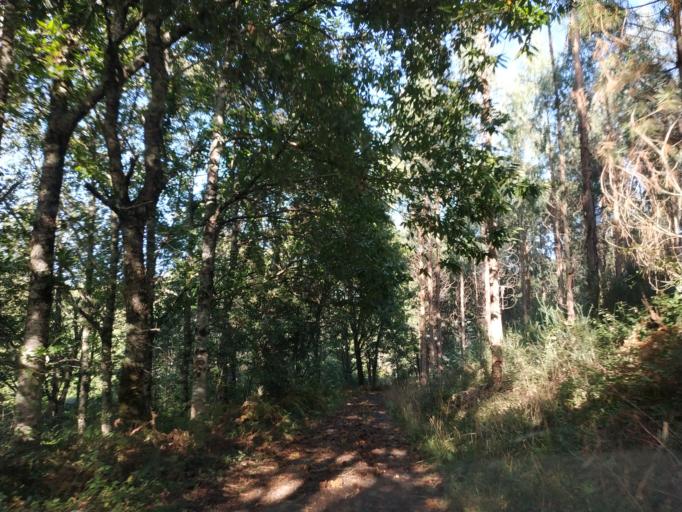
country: ES
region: Galicia
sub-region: Provincia da Coruna
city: Negreira
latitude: 42.9154
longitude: -8.7575
